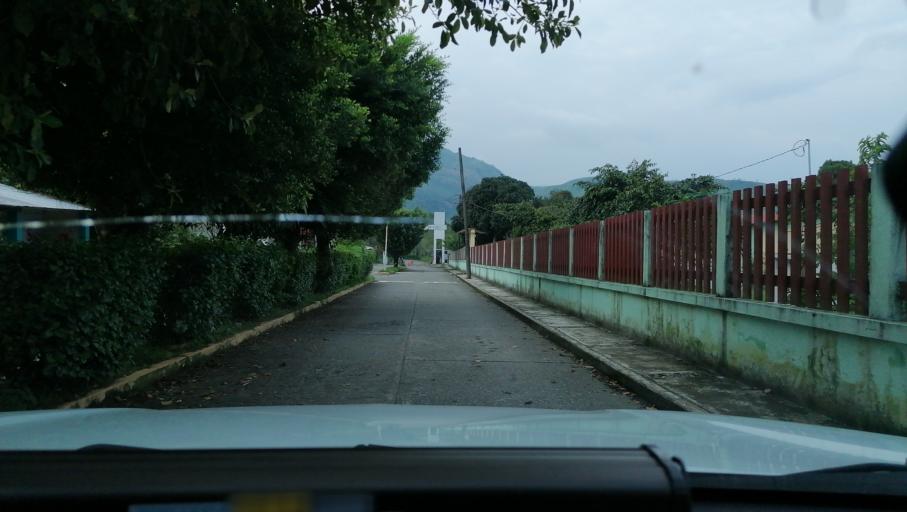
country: MX
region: Chiapas
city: Ixtacomitan
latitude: 17.3432
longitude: -93.1308
